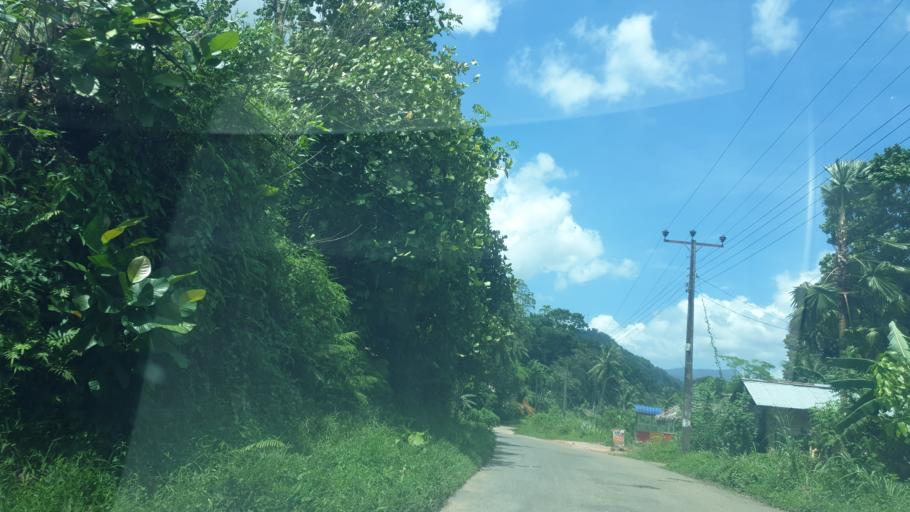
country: LK
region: Sabaragamuwa
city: Ratnapura
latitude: 6.4720
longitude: 80.4220
